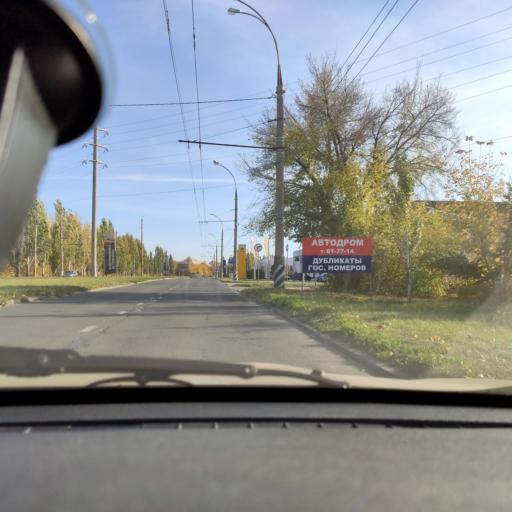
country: RU
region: Samara
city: Tol'yatti
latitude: 53.5464
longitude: 49.2753
